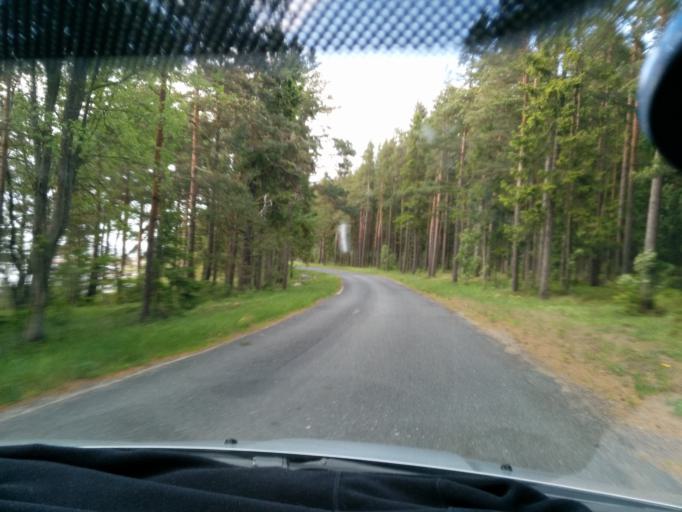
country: EE
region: Harju
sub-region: Loksa linn
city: Loksa
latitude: 59.6262
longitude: 25.6862
